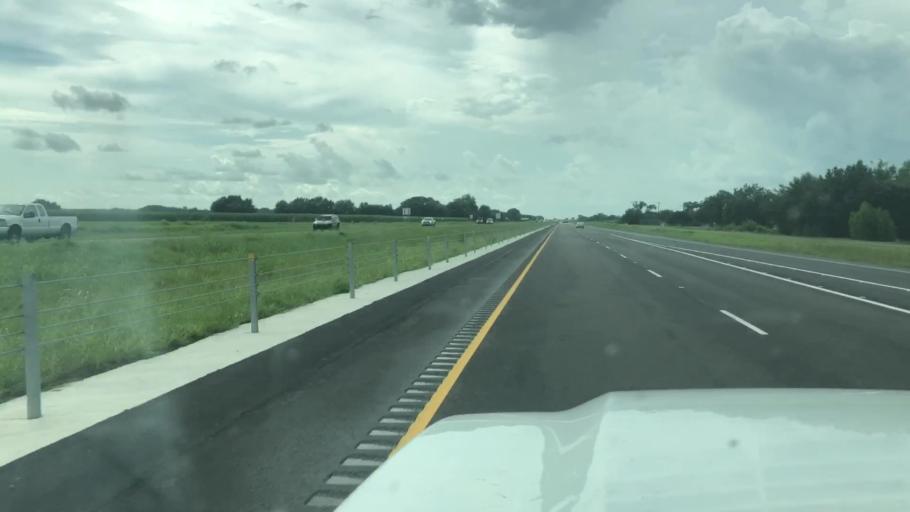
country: US
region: Louisiana
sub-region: Iberia Parish
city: Jeanerette
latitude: 29.8687
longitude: -91.6377
